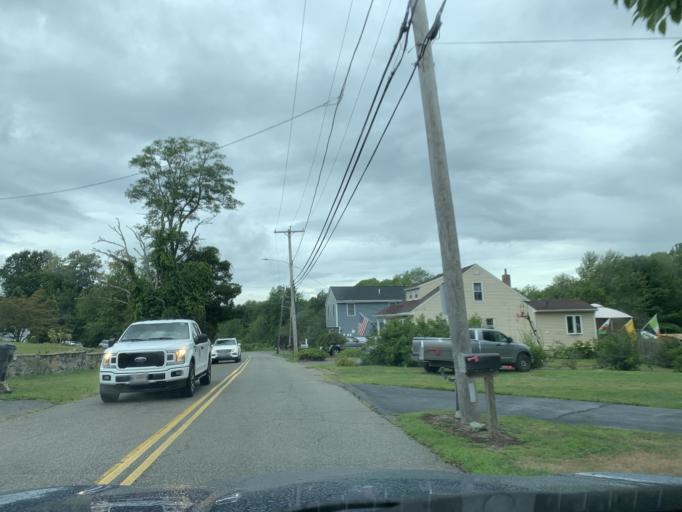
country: US
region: Rhode Island
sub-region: Bristol County
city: Warren
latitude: 41.7406
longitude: -71.2674
